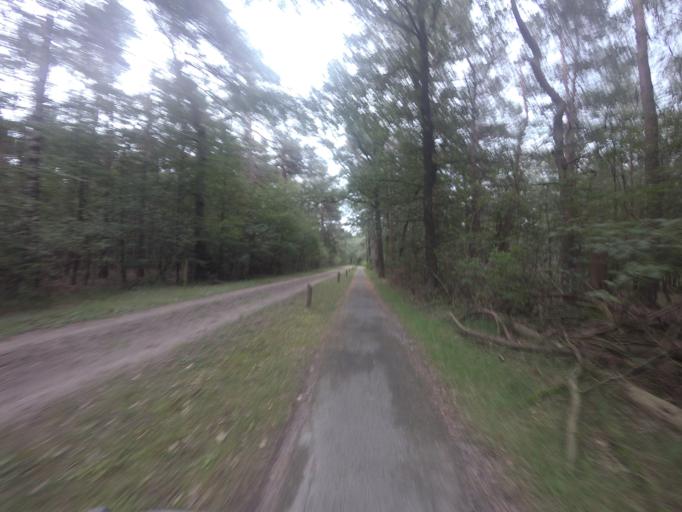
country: NL
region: Drenthe
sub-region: Gemeente Westerveld
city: Dwingeloo
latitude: 52.8762
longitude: 6.2758
